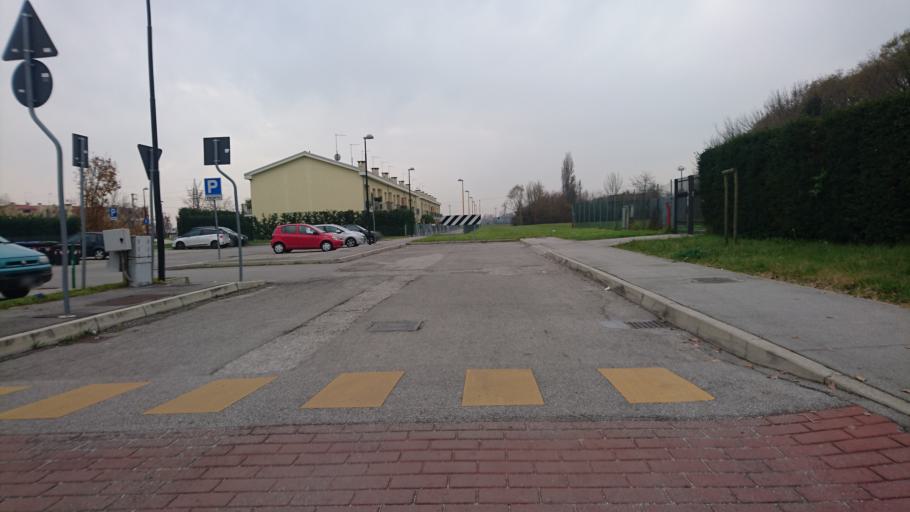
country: IT
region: Veneto
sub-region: Provincia di Padova
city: Ponte San Nicolo
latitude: 45.3650
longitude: 11.9250
